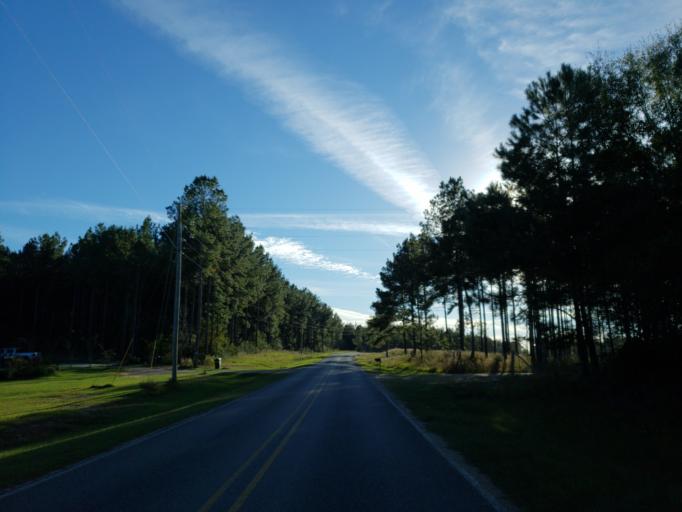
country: US
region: Mississippi
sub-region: Perry County
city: Richton
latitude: 31.3422
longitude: -88.7901
